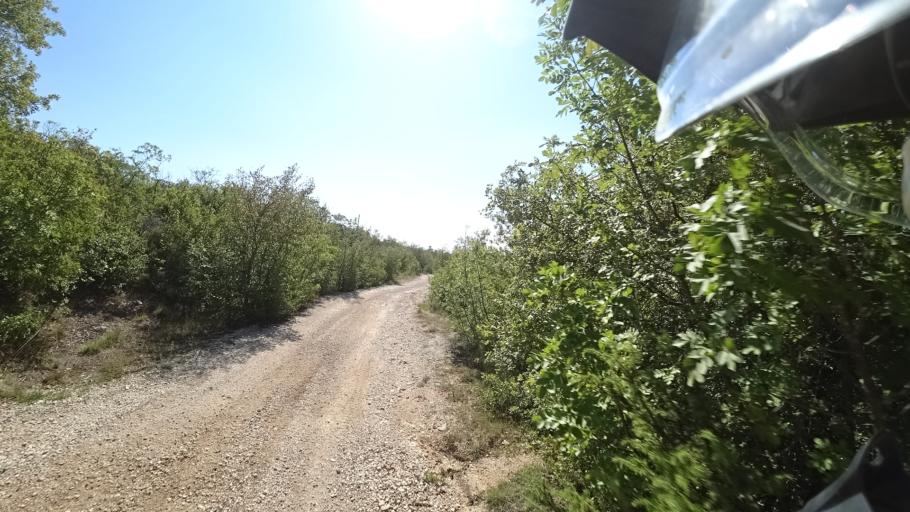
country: HR
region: Sibensko-Kniniska
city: Drnis
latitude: 43.9114
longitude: 16.1710
